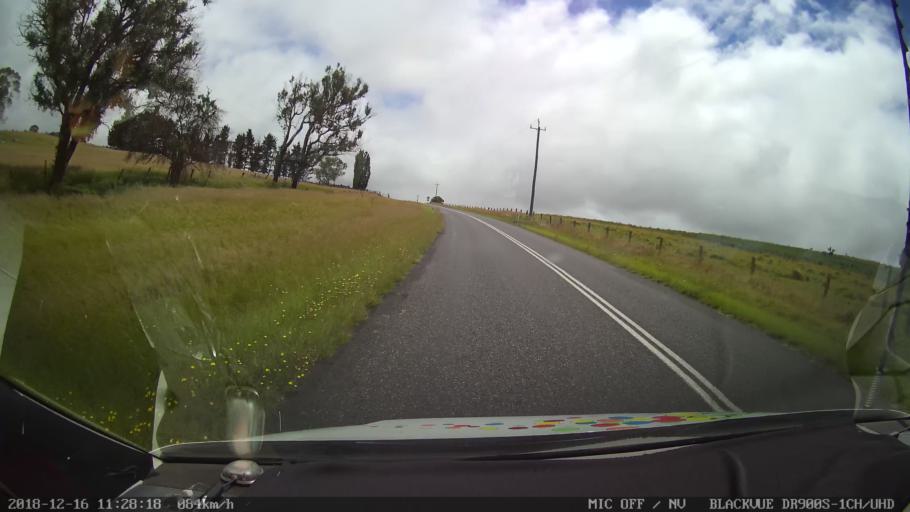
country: AU
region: New South Wales
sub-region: Tenterfield Municipality
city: Carrolls Creek
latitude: -29.0406
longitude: 152.0970
